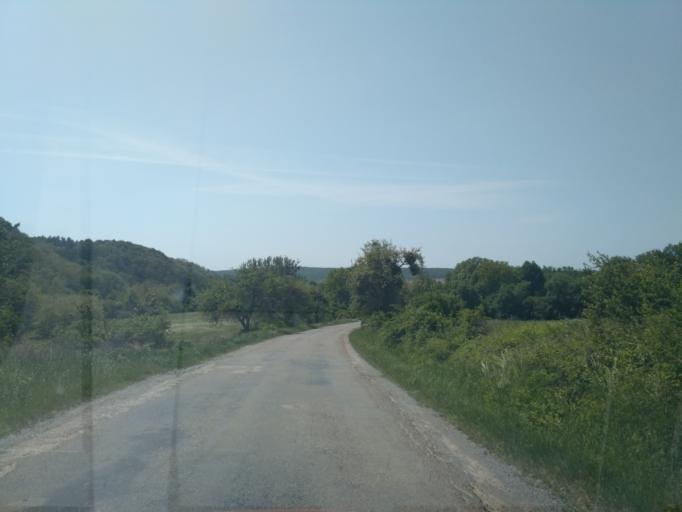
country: SK
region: Kosicky
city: Kosice
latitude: 48.7876
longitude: 21.3430
